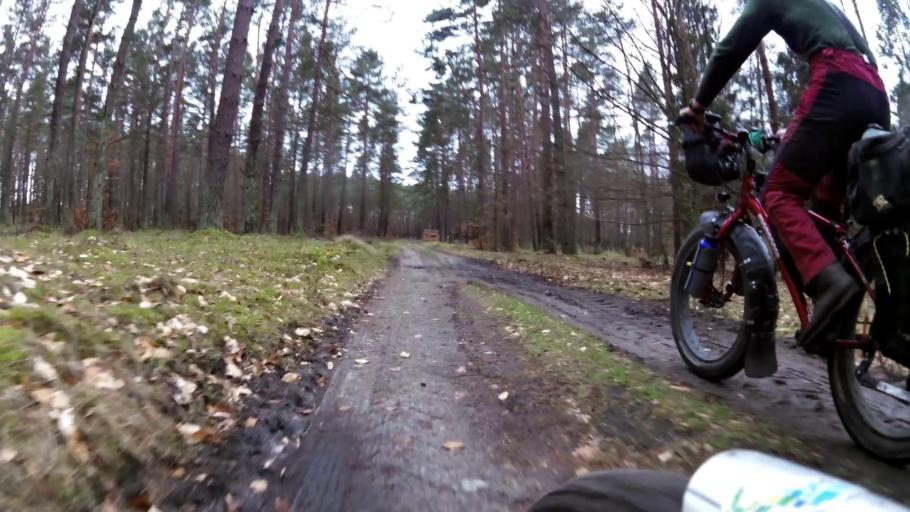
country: PL
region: Pomeranian Voivodeship
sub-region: Powiat bytowski
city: Trzebielino
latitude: 54.1340
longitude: 17.1433
